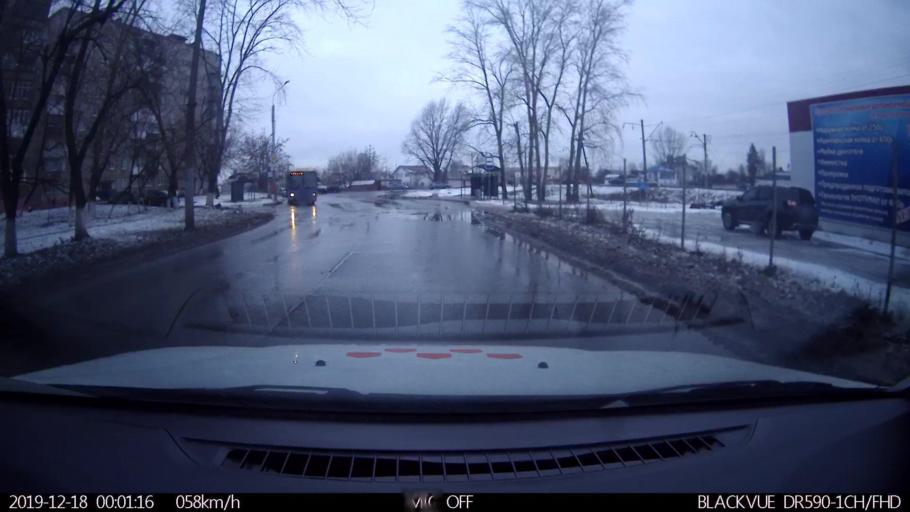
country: RU
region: Nizjnij Novgorod
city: Gorbatovka
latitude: 56.3698
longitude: 43.8245
